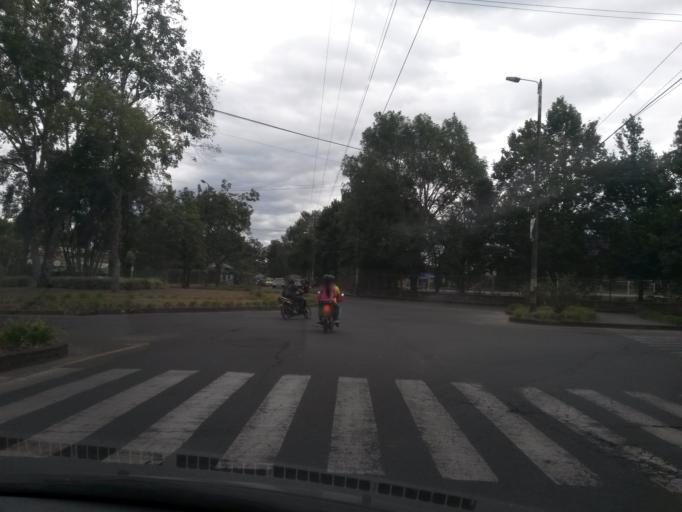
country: CO
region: Cauca
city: Popayan
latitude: 2.4597
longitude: -76.5992
